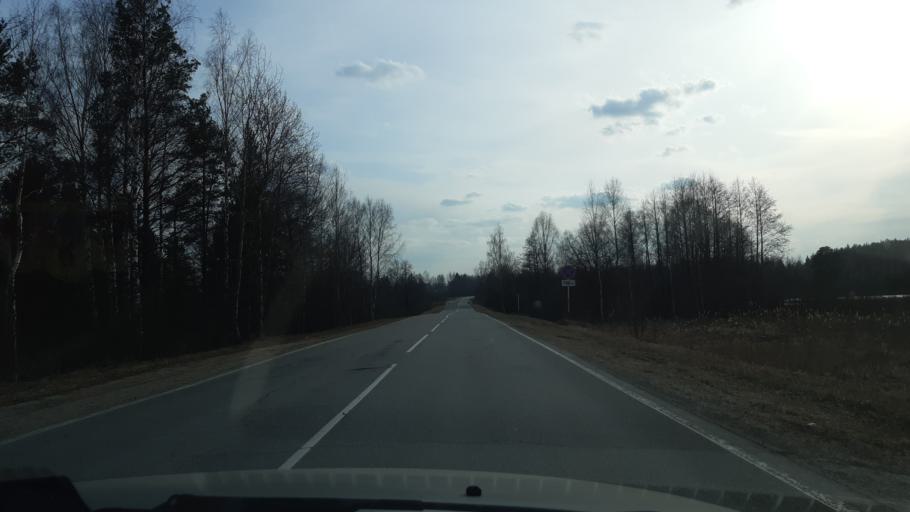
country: RU
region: Vladimir
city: Luknovo
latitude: 56.1809
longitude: 42.0117
